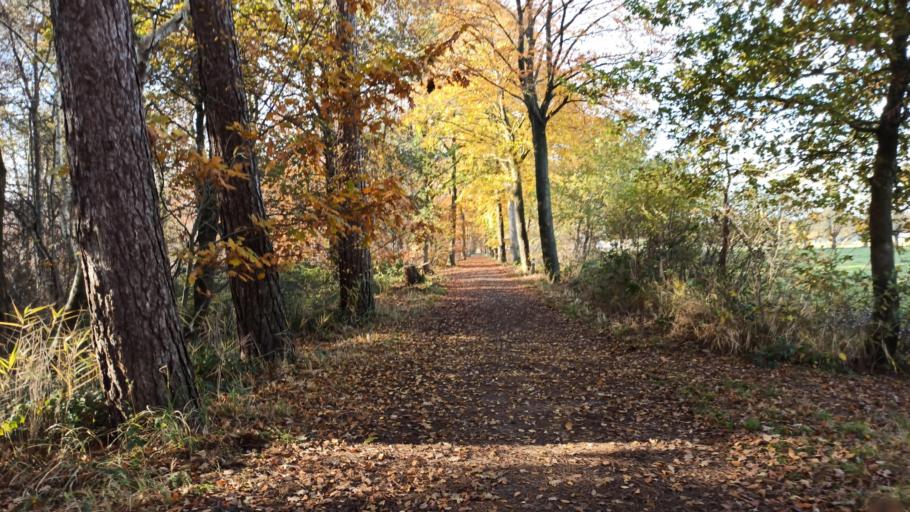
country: BE
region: Flanders
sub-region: Provincie Oost-Vlaanderen
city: Maldegem
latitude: 51.1640
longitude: 3.4515
